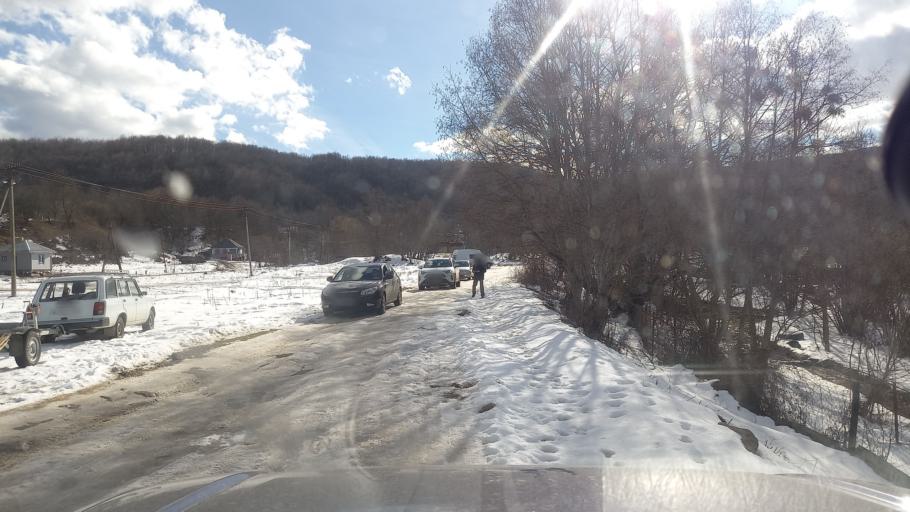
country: RU
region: Adygeya
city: Kamennomostskiy
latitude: 44.1964
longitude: 39.9605
